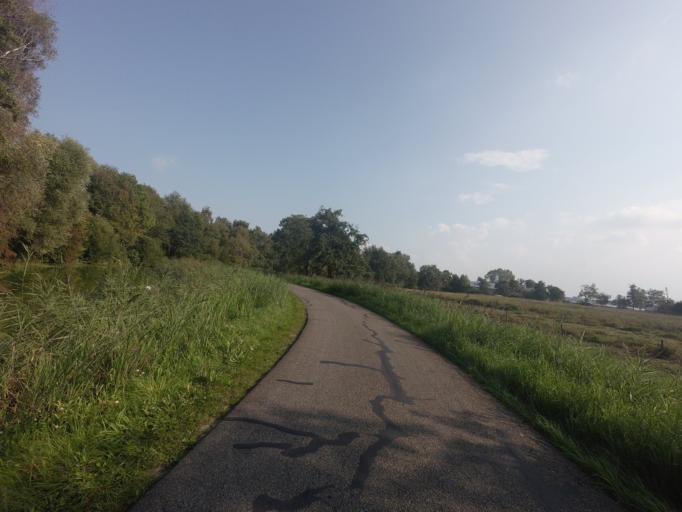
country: NL
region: Groningen
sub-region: Gemeente Haren
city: Haren
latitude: 53.1791
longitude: 6.5756
